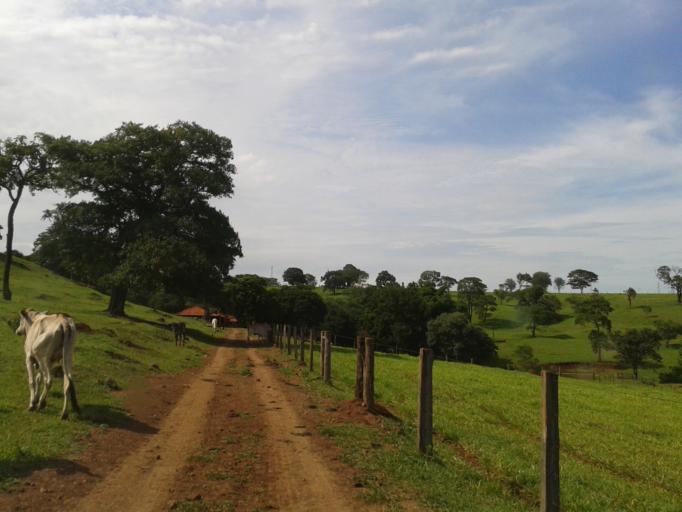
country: BR
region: Minas Gerais
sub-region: Centralina
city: Centralina
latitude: -18.7021
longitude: -49.2085
